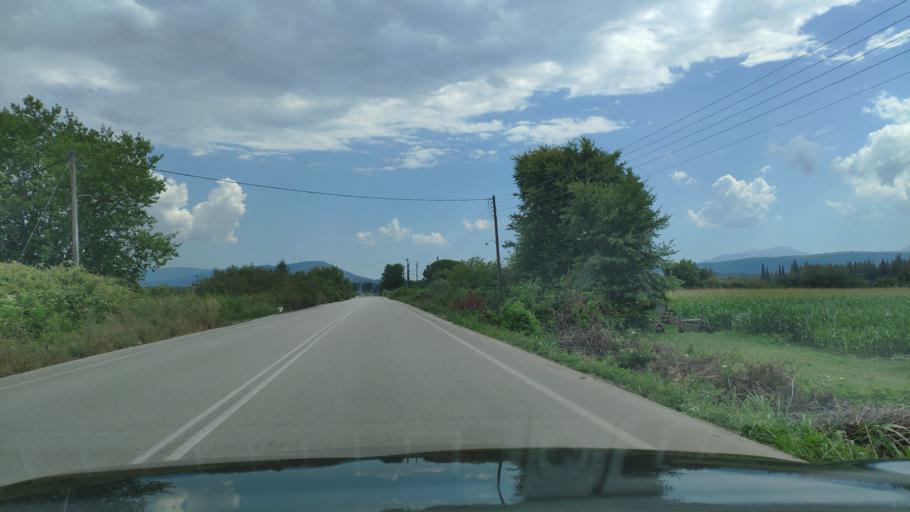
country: GR
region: West Greece
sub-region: Nomos Aitolias kai Akarnanias
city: Krikellos
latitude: 38.9363
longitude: 21.1770
